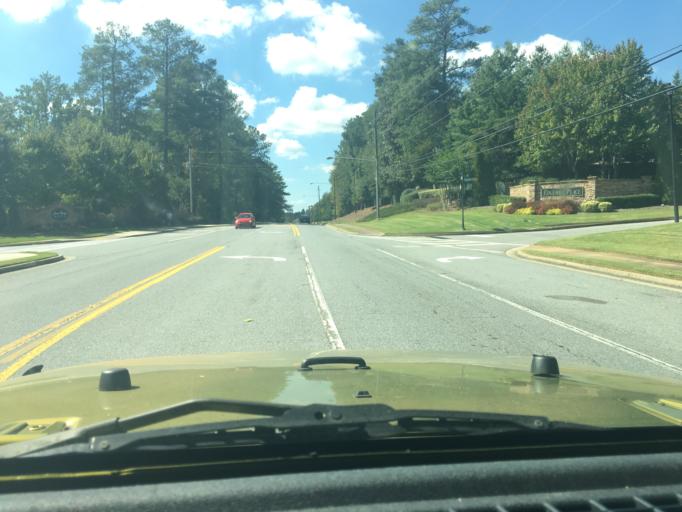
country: US
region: Georgia
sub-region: Fulton County
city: Johns Creek
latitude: 34.0399
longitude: -84.2305
